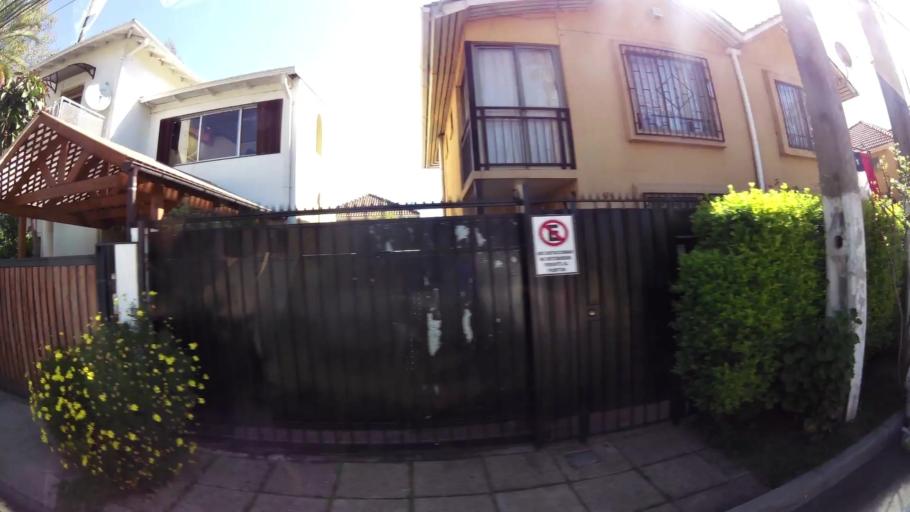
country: CL
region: Santiago Metropolitan
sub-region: Provincia de Talagante
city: Penaflor
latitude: -33.6047
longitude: -70.9014
